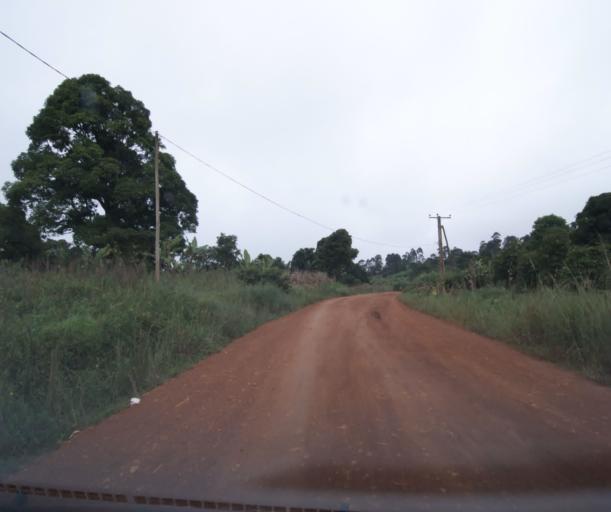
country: CM
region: West
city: Dschang
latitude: 5.5109
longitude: 9.9847
